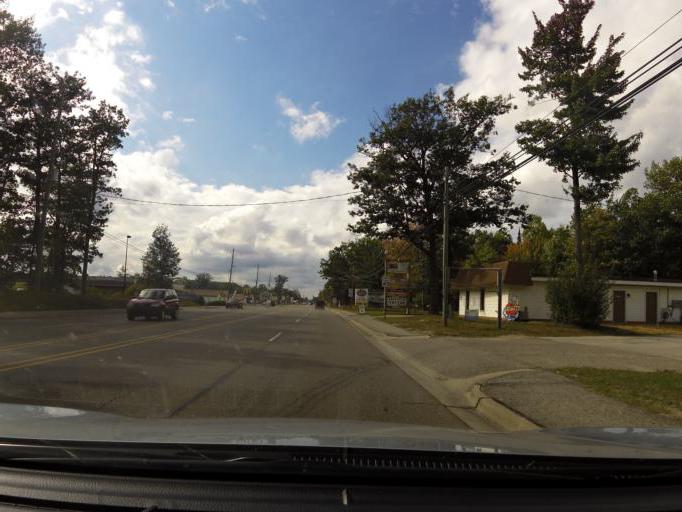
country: US
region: Michigan
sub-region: Roscommon County
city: Prudenville
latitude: 44.2987
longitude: -84.6764
